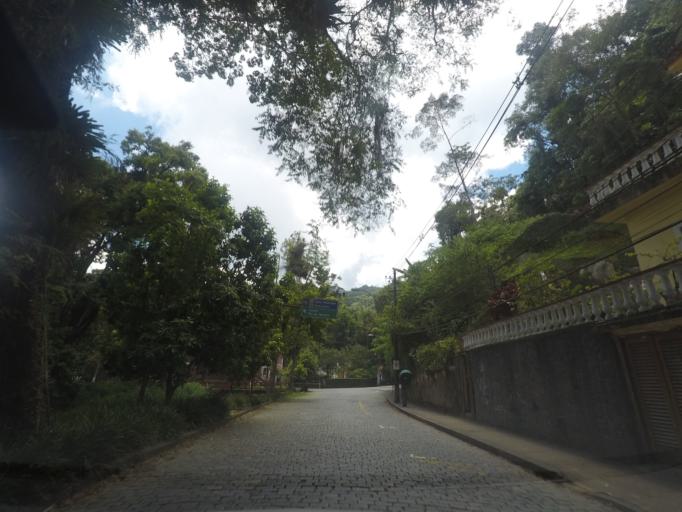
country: BR
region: Rio de Janeiro
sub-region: Petropolis
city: Petropolis
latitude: -22.5035
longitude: -43.1849
